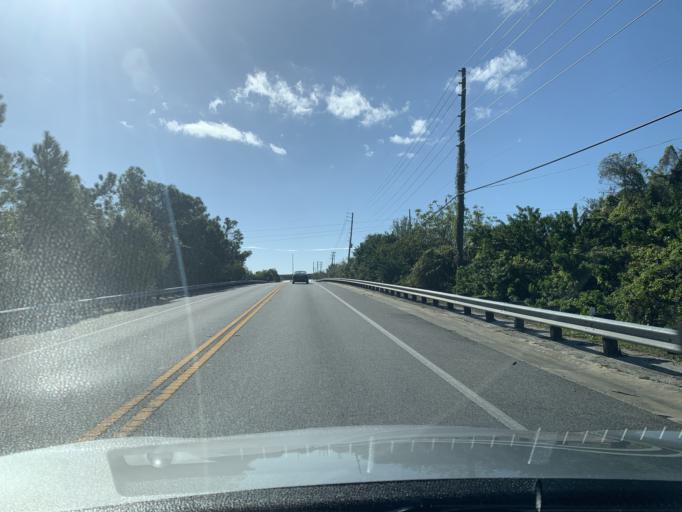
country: US
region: Florida
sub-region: Orange County
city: Lockhart
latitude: 28.6359
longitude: -81.4588
